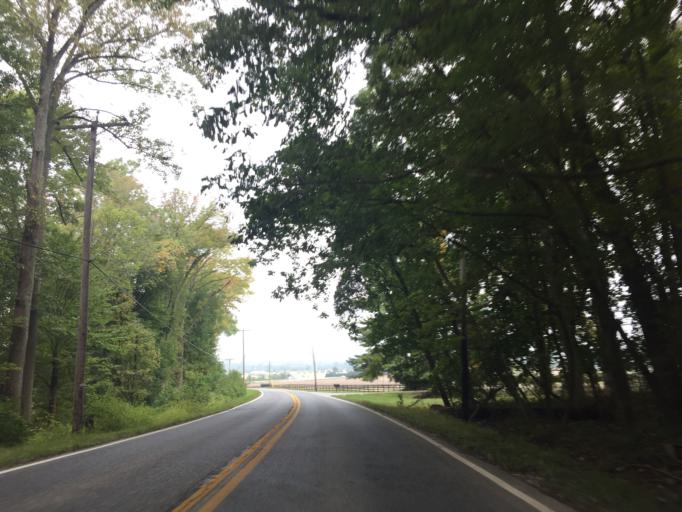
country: US
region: Maryland
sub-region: Baltimore County
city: Owings Mills
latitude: 39.4734
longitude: -76.7583
